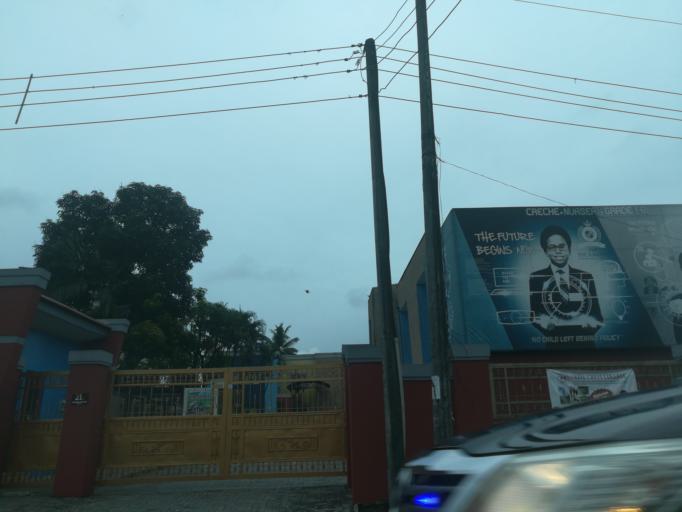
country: NG
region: Rivers
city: Port Harcourt
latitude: 4.8164
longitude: 6.9982
